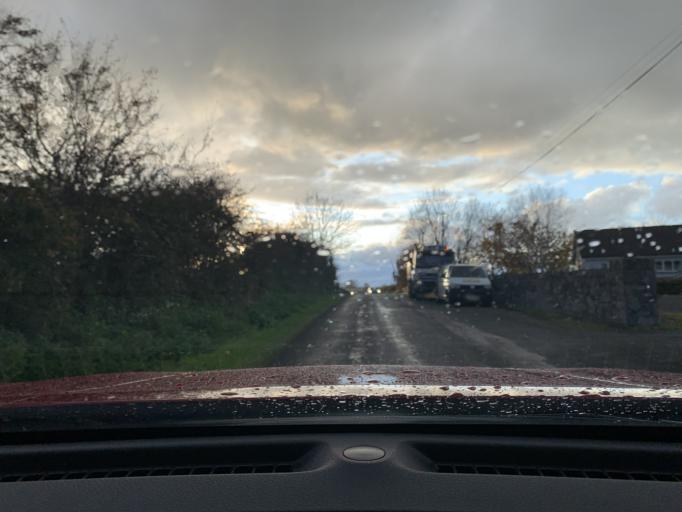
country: IE
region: Connaught
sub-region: Sligo
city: Sligo
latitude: 54.3114
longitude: -8.4968
